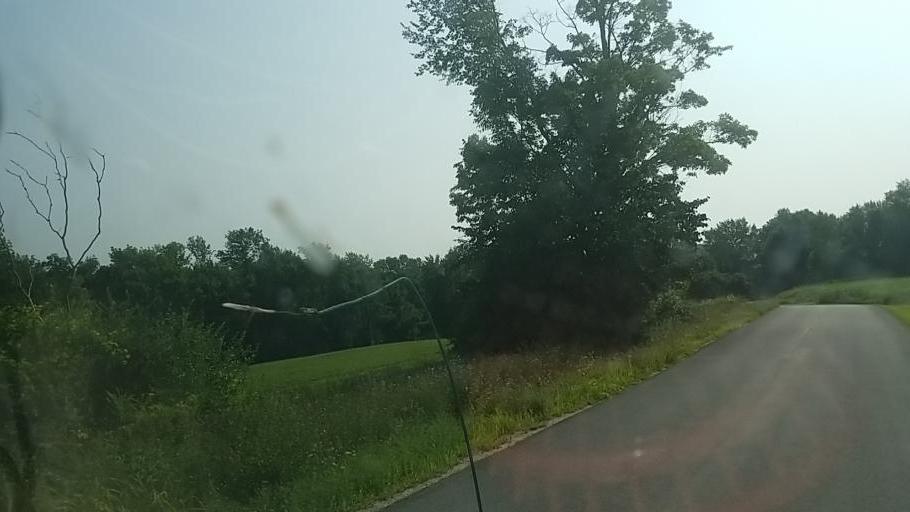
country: US
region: New York
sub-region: Montgomery County
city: Fonda
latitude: 42.9155
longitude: -74.3471
